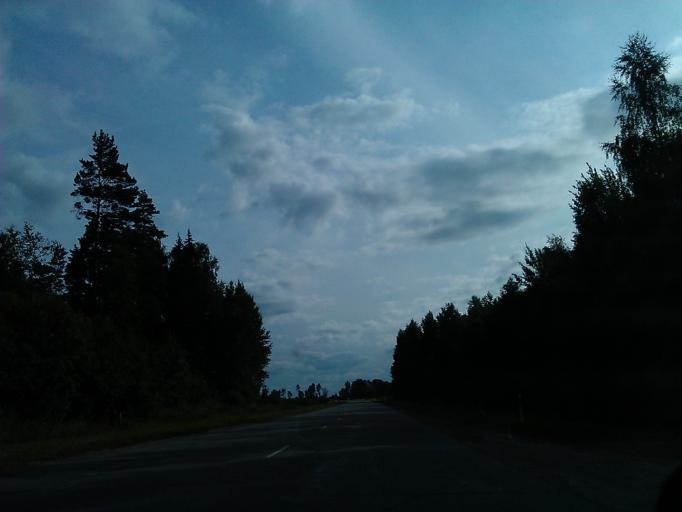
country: LV
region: Cesu Rajons
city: Cesis
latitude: 57.2786
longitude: 25.2864
